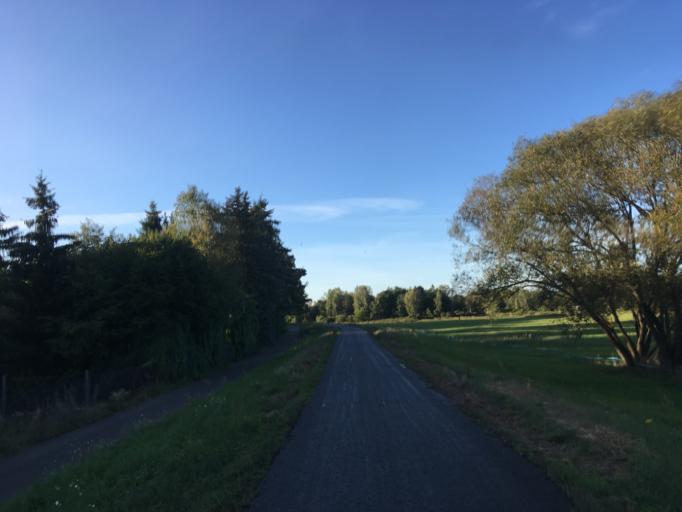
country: PL
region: Lubusz
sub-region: Powiat zarski
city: Trzebiel
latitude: 51.6744
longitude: 14.7466
